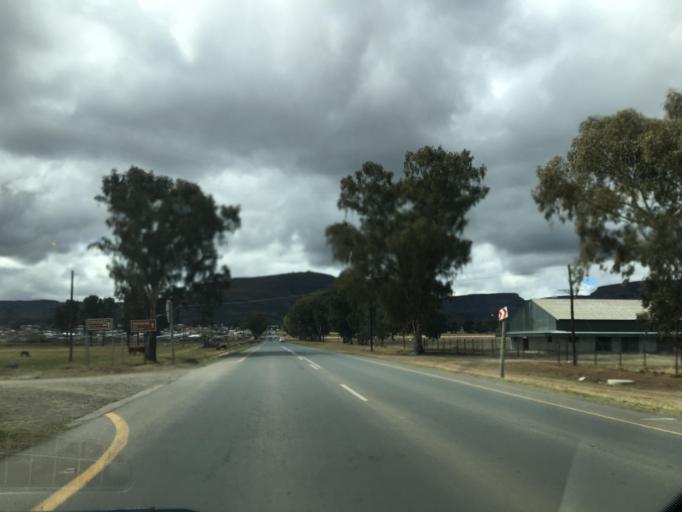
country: ZA
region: Eastern Cape
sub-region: Chris Hani District Municipality
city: Cala
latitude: -31.5298
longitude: 27.6793
